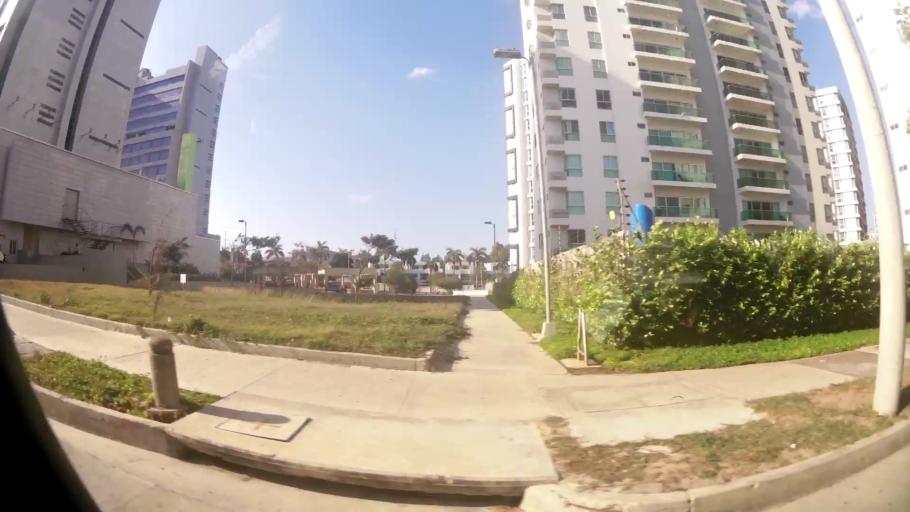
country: CO
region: Atlantico
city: Barranquilla
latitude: 11.0171
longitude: -74.8317
